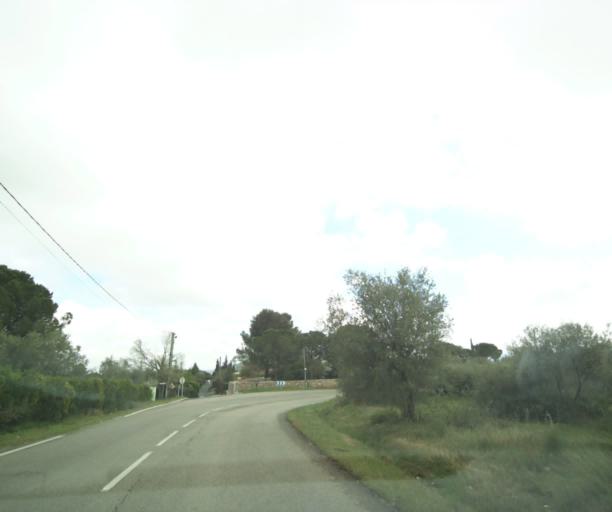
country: FR
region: Languedoc-Roussillon
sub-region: Departement de l'Herault
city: Pignan
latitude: 43.5897
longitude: 3.7533
